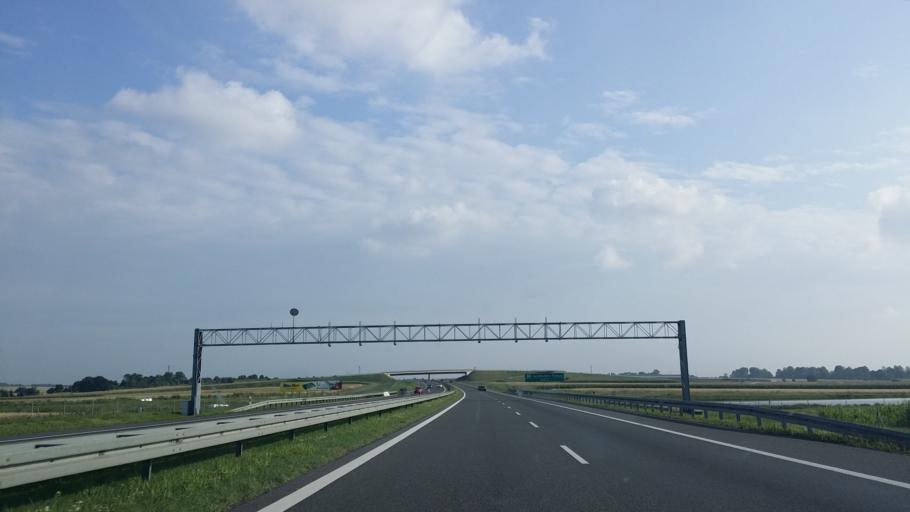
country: PL
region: Lubusz
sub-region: Powiat swiebodzinski
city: Swiebodzin
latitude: 52.3067
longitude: 15.5440
